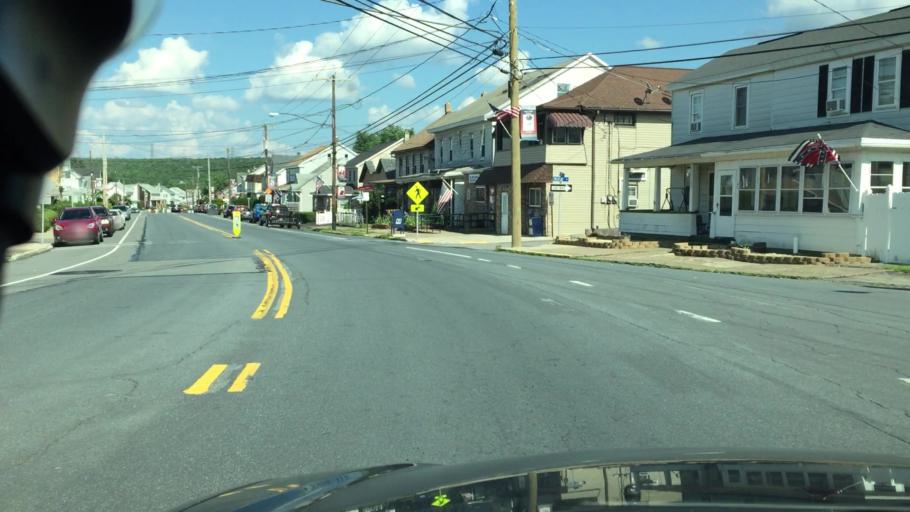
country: US
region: Pennsylvania
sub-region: Luzerne County
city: Oakdale
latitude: 40.9284
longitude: -75.9151
